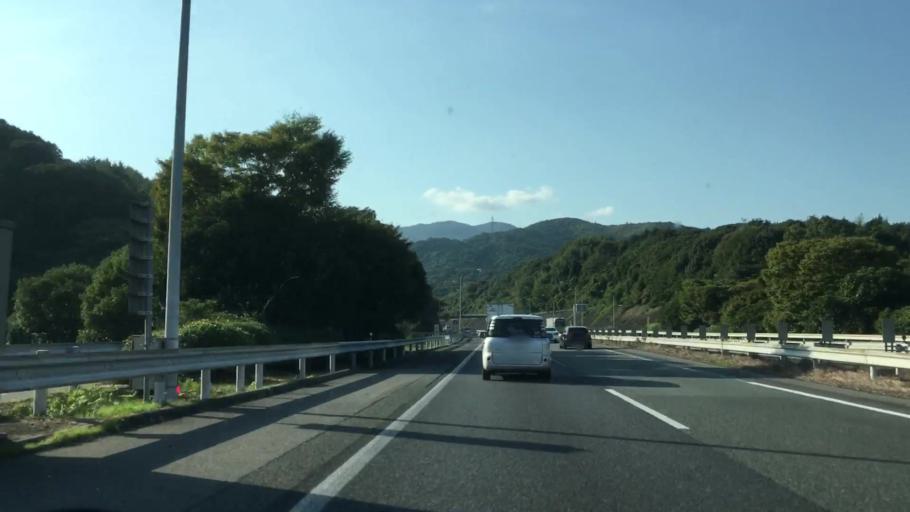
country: JP
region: Yamaguchi
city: Hofu
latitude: 34.0695
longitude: 131.6858
